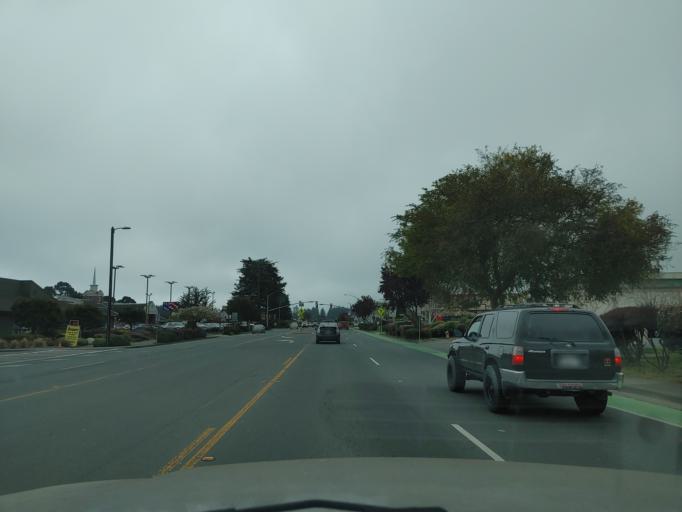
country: US
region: California
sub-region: Humboldt County
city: McKinleyville
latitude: 40.9409
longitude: -124.1010
